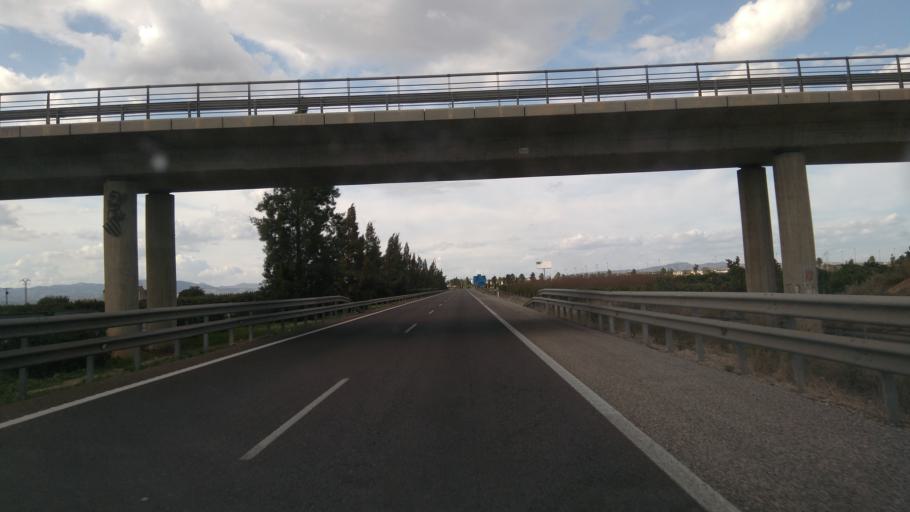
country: ES
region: Valencia
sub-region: Provincia de Valencia
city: Guadassuar
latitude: 39.1705
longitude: -0.4639
